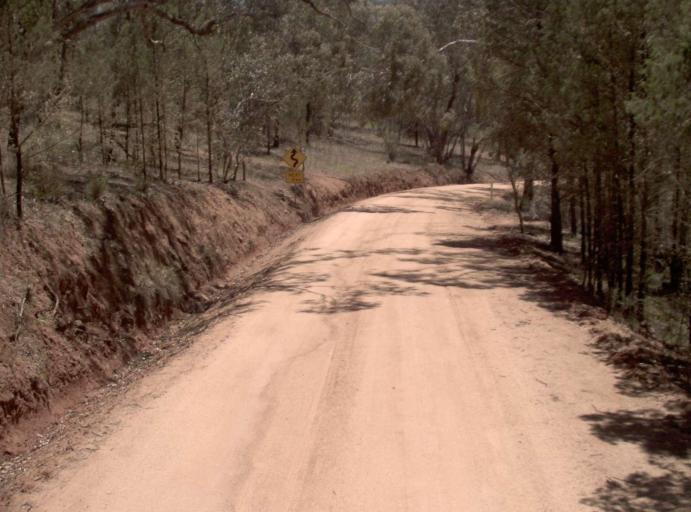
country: AU
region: New South Wales
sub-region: Snowy River
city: Jindabyne
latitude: -36.9550
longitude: 148.3238
